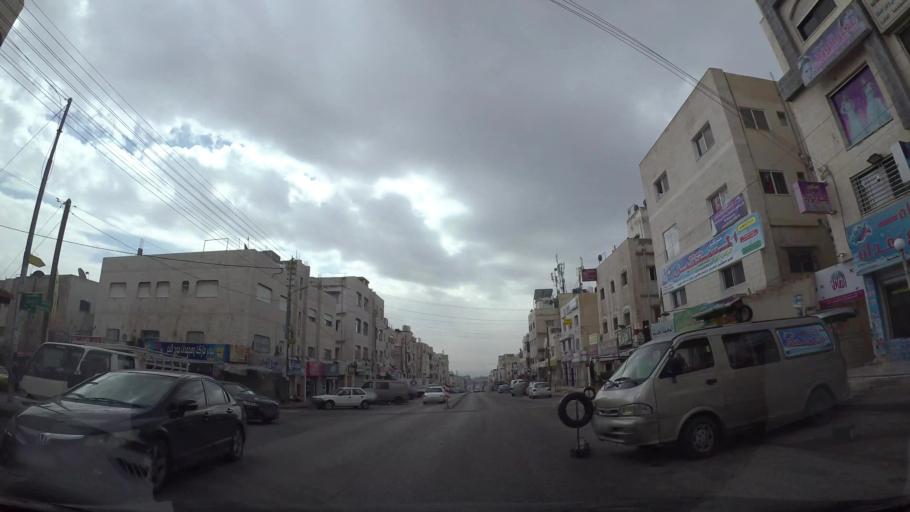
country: JO
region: Amman
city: Amman
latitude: 31.9842
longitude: 35.9241
